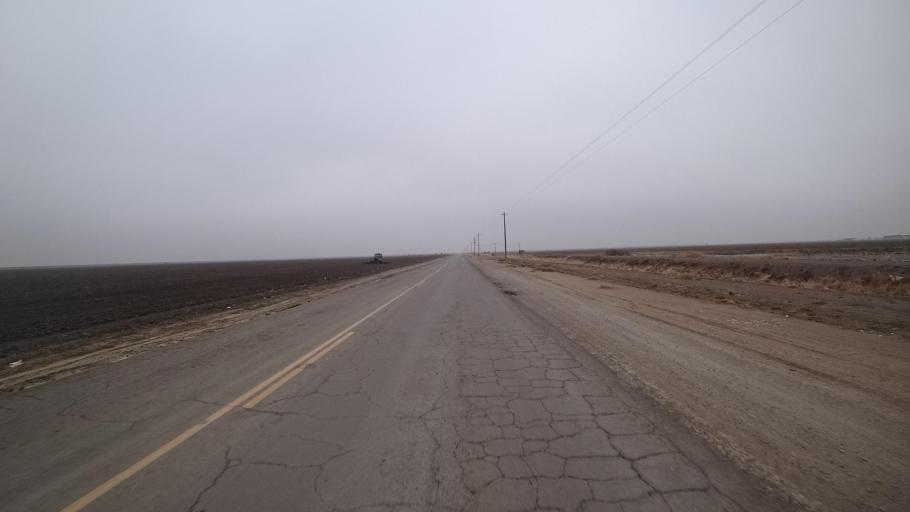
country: US
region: California
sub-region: Kern County
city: Rosedale
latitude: 35.1786
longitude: -119.1991
